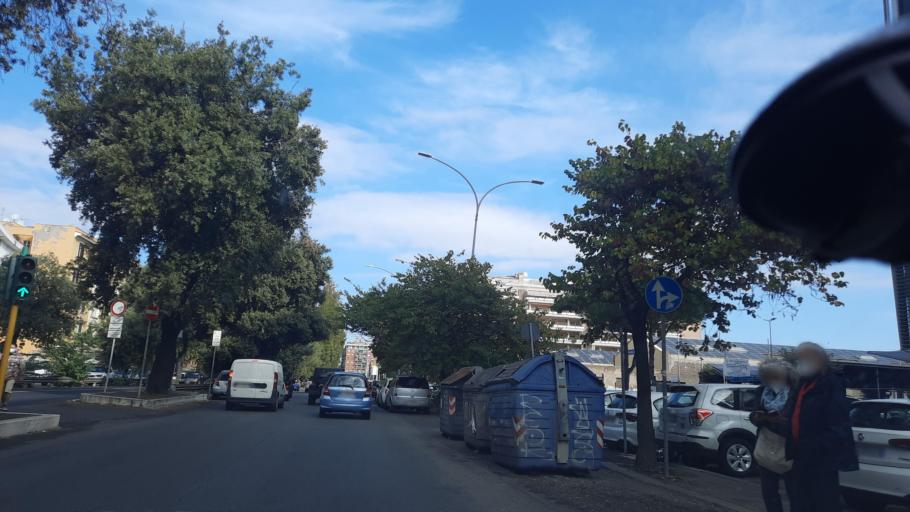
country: IT
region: Latium
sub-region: Citta metropolitana di Roma Capitale
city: Rome
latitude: 41.8656
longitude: 12.4792
